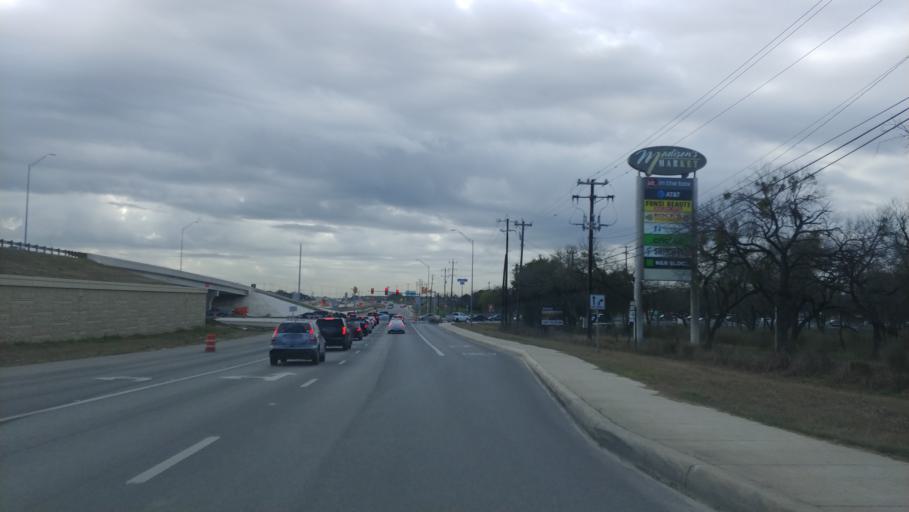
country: US
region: Texas
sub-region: Bexar County
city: Lackland Air Force Base
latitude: 29.4370
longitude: -98.7120
